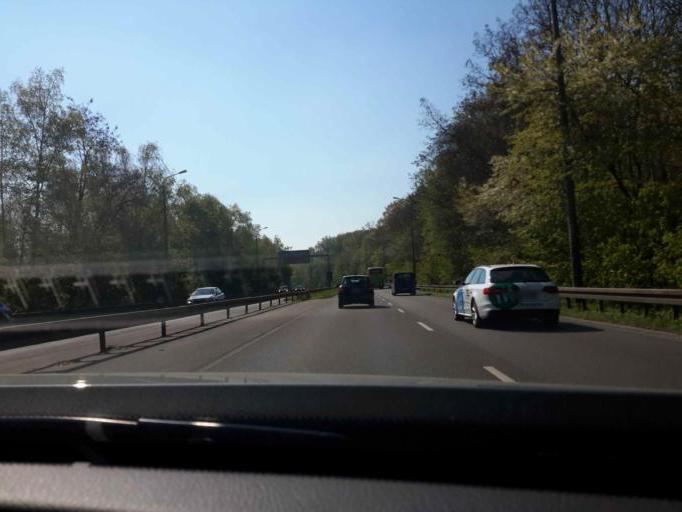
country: DE
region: Saxony
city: Leipzig
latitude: 51.3080
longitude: 12.3659
